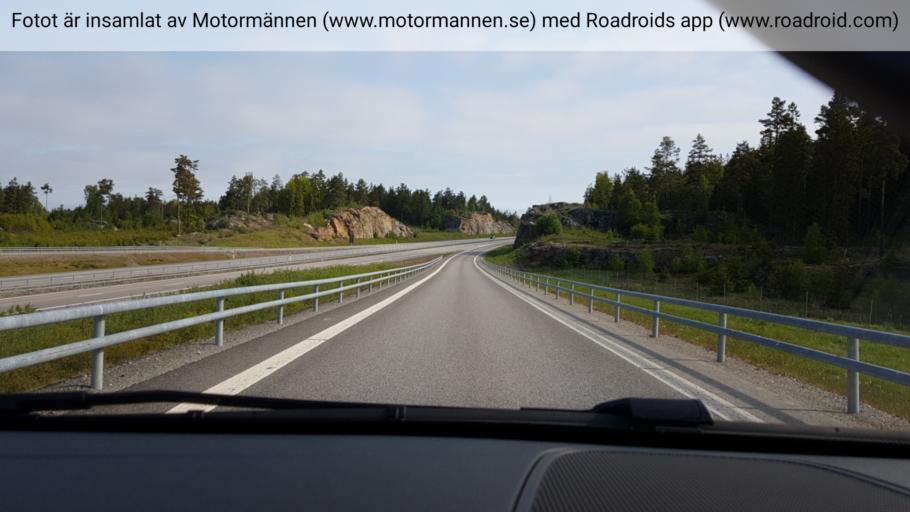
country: SE
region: Stockholm
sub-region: Nynashamns Kommun
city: Osmo
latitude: 59.0267
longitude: 17.9525
